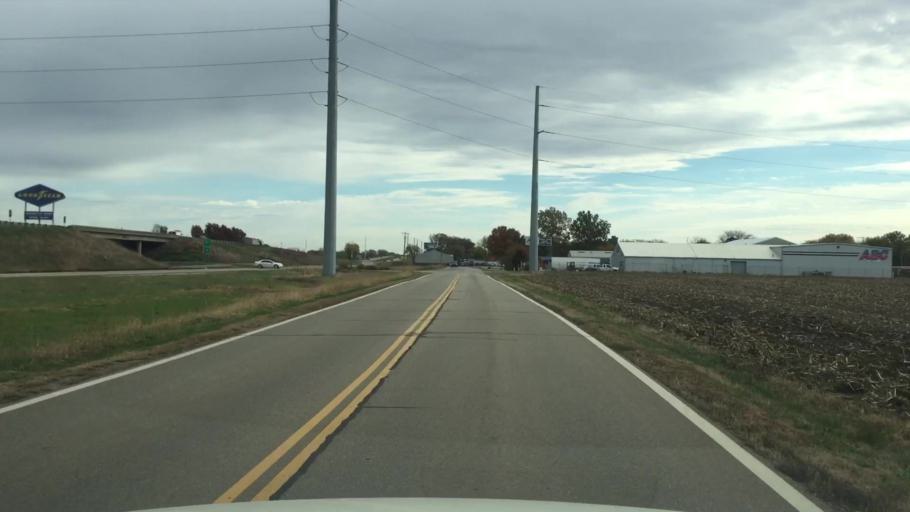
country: US
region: Kansas
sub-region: Shawnee County
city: Topeka
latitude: 39.0902
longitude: -95.6985
